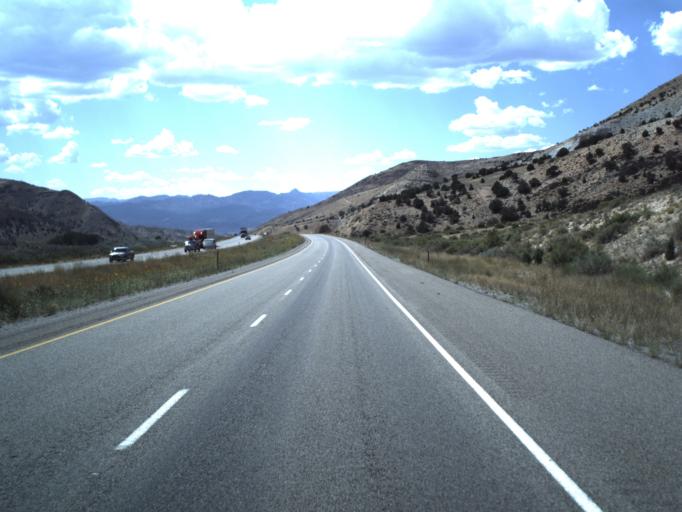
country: US
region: Utah
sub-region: Sevier County
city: Salina
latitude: 38.9331
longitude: -111.7978
